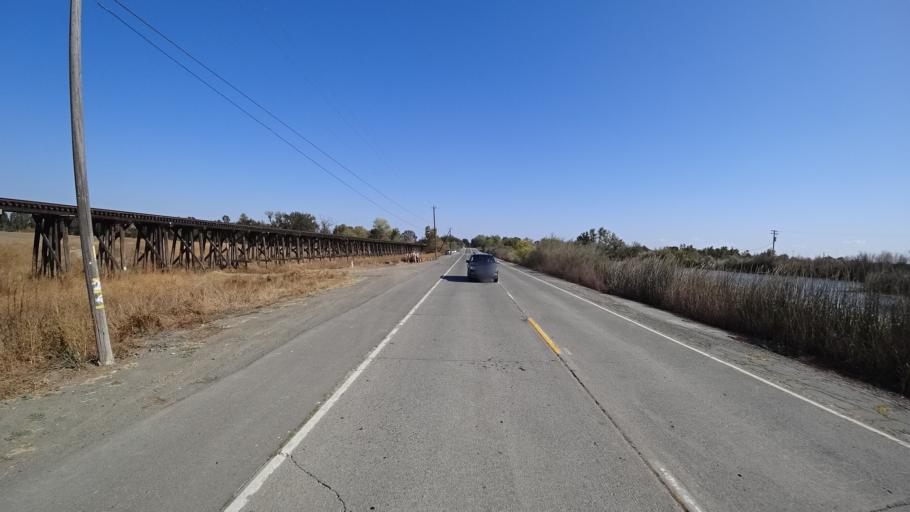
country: US
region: California
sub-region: Yolo County
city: Woodland
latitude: 38.6767
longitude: -121.6474
